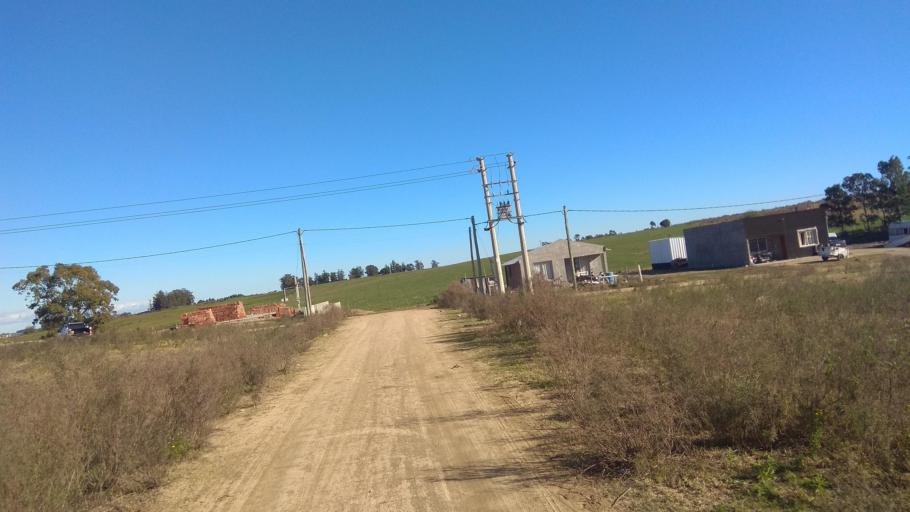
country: UY
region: Florida
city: Florida
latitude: -34.0812
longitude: -56.2399
